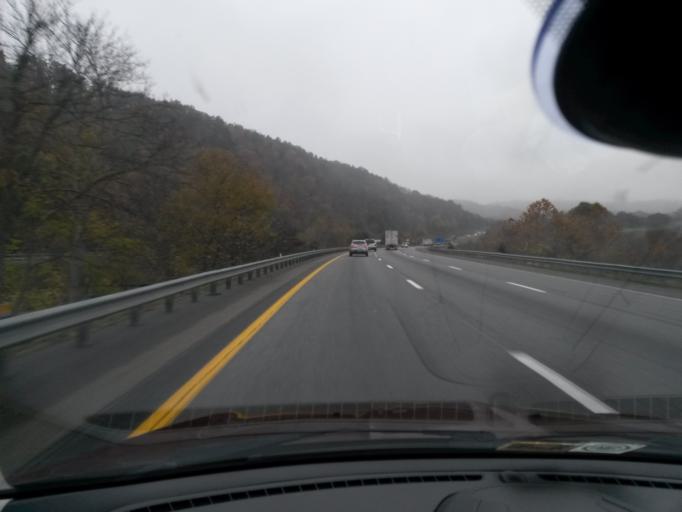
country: US
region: Virginia
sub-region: Montgomery County
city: Shawsville
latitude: 37.2371
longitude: -80.2336
